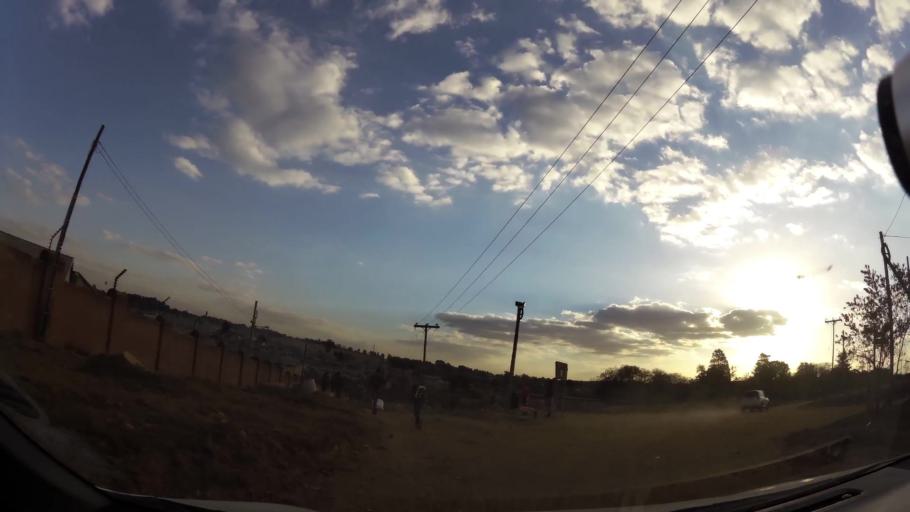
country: ZA
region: Gauteng
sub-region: City of Johannesburg Metropolitan Municipality
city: Diepsloot
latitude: -26.0060
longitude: 27.9713
